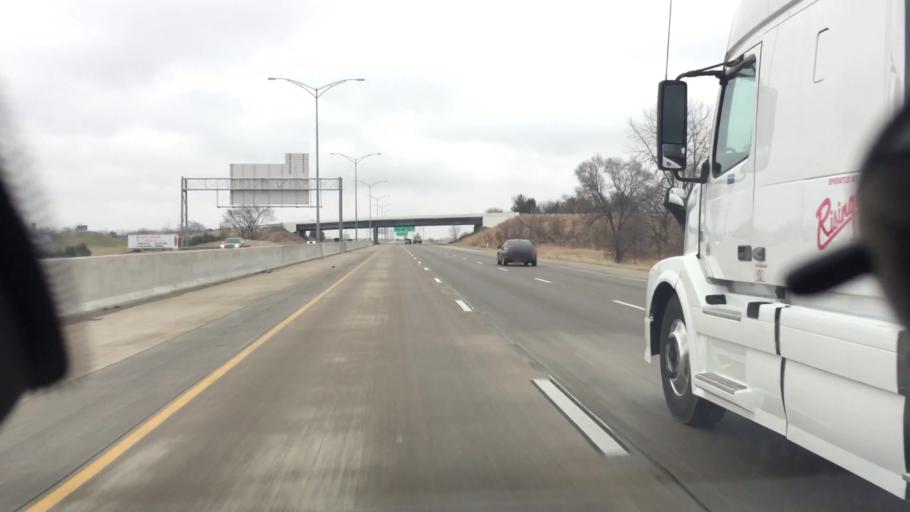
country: US
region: Illinois
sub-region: Tazewell County
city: Morton
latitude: 40.6278
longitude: -89.5039
